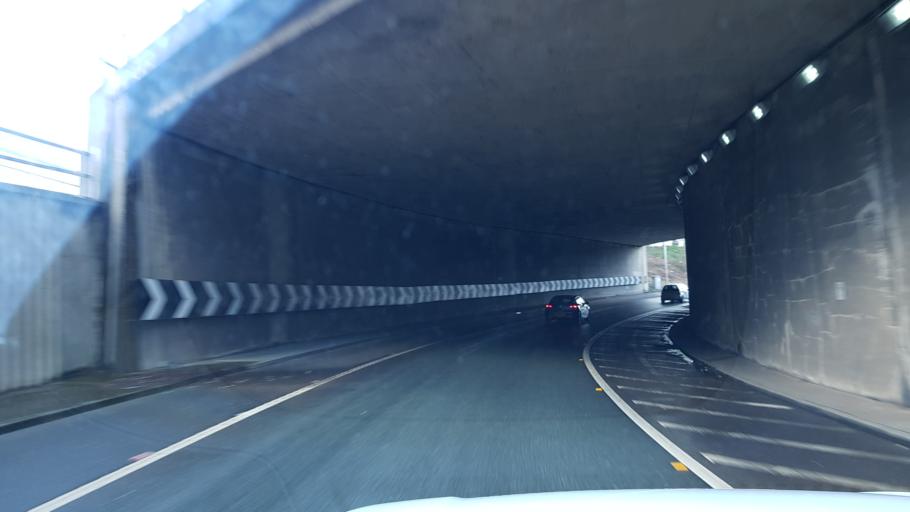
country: GB
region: England
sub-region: Liverpool
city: Liverpool
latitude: 53.4181
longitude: -2.9823
